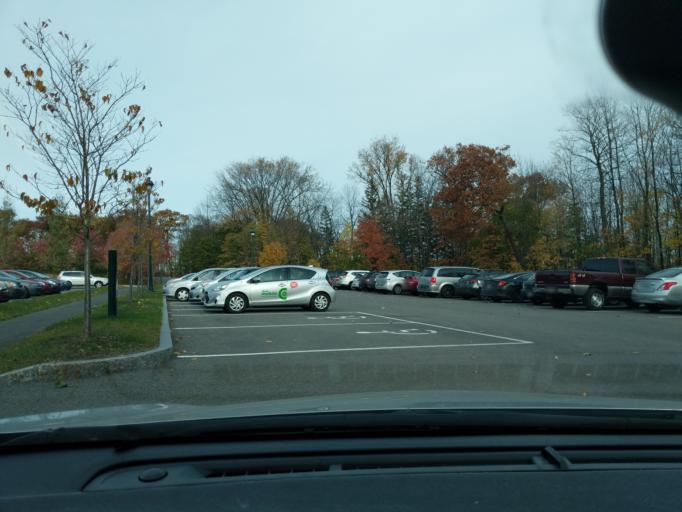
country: CA
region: Quebec
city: Quebec
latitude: 46.7741
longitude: -71.2530
